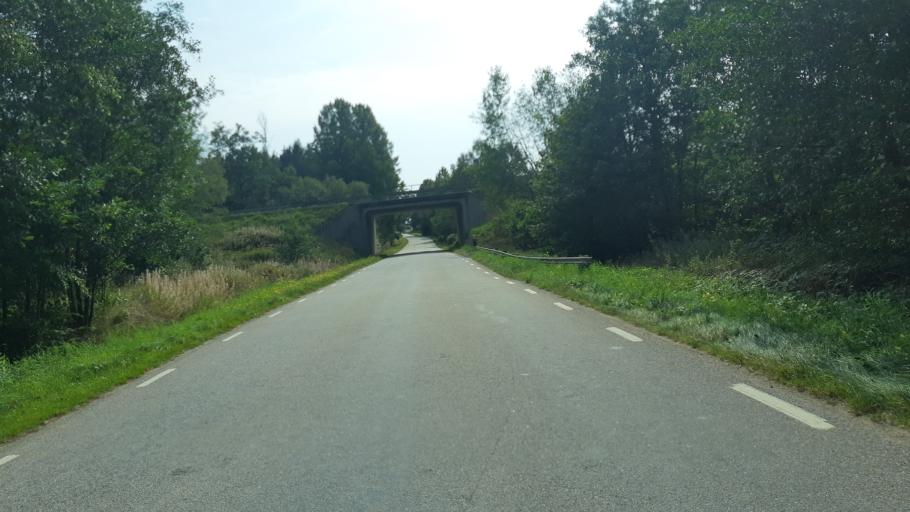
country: SE
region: Blekinge
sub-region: Ronneby Kommun
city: Kallinge
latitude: 56.2053
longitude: 15.3420
